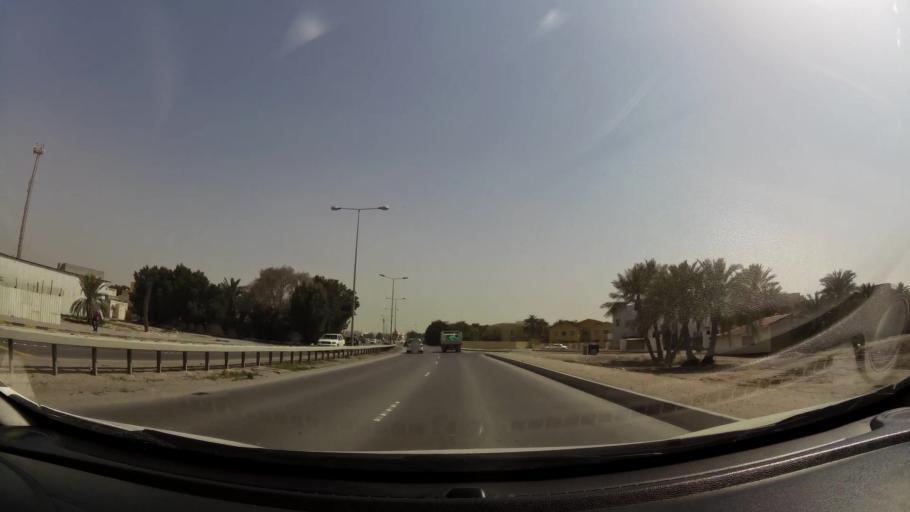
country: BH
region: Northern
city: Madinat `Isa
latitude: 26.1959
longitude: 50.4617
